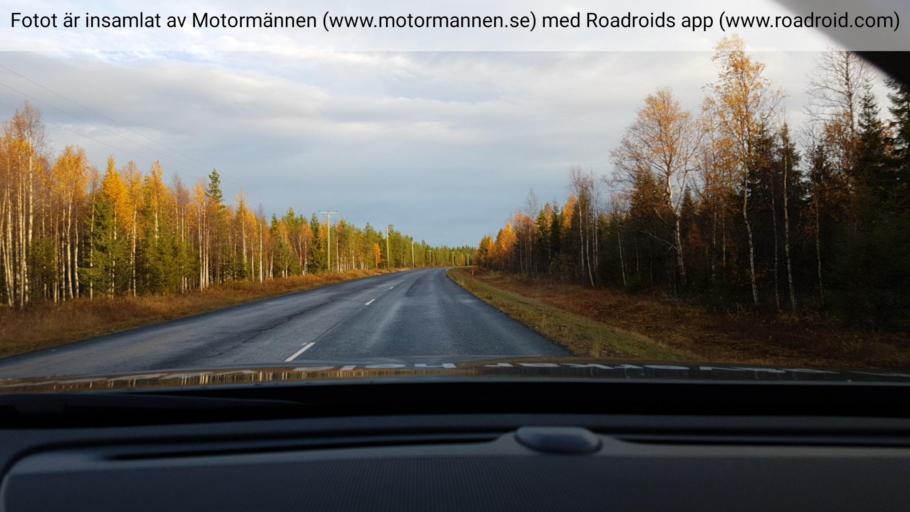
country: SE
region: Norrbotten
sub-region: Overkalix Kommun
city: OEverkalix
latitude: 66.9653
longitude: 22.6728
